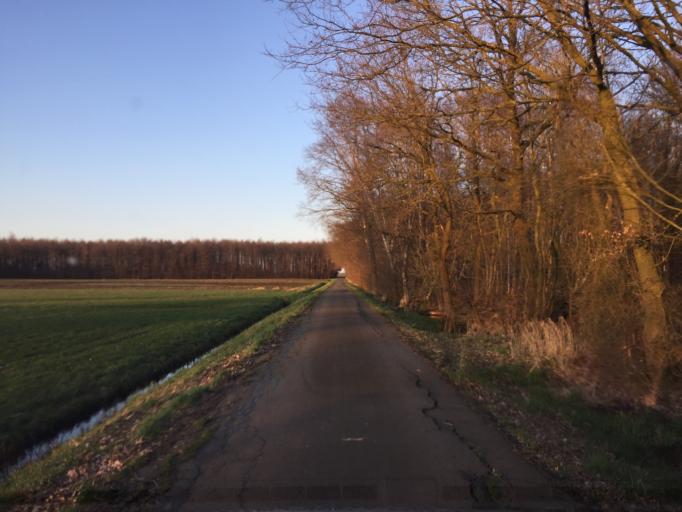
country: DE
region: Lower Saxony
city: Varrel
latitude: 52.6672
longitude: 8.7565
